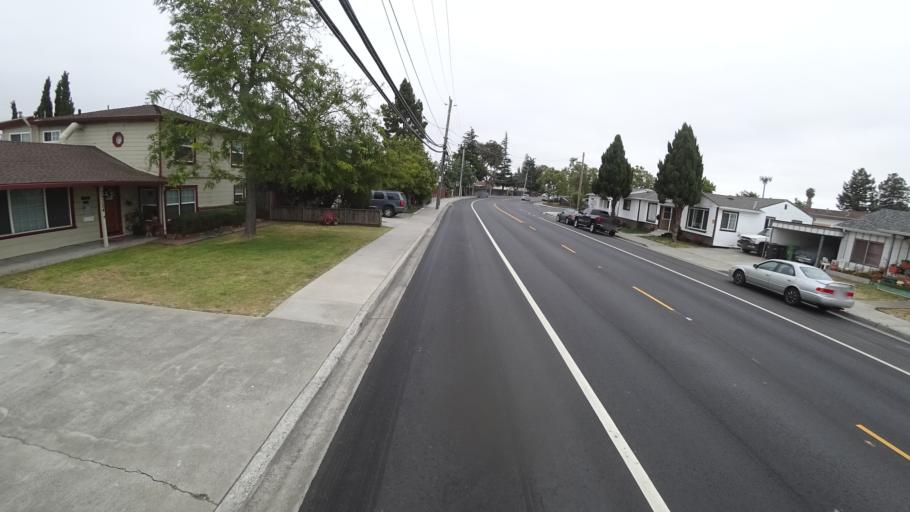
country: US
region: California
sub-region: Alameda County
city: Hayward
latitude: 37.6219
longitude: -122.0643
